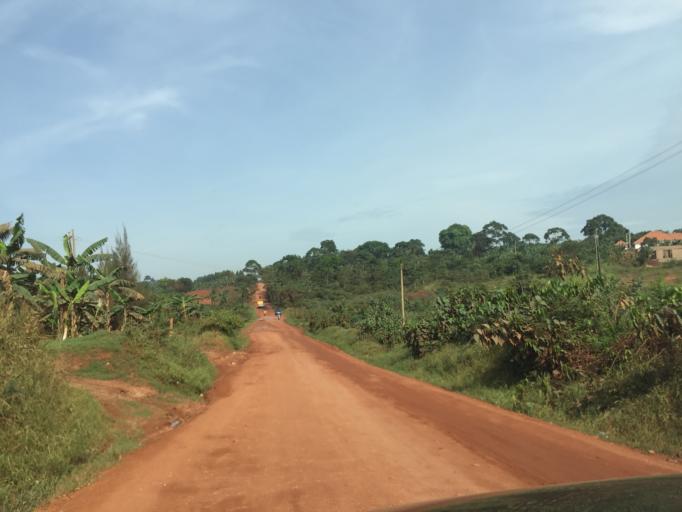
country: UG
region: Central Region
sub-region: Wakiso District
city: Wakiso
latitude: 0.4528
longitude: 32.5714
